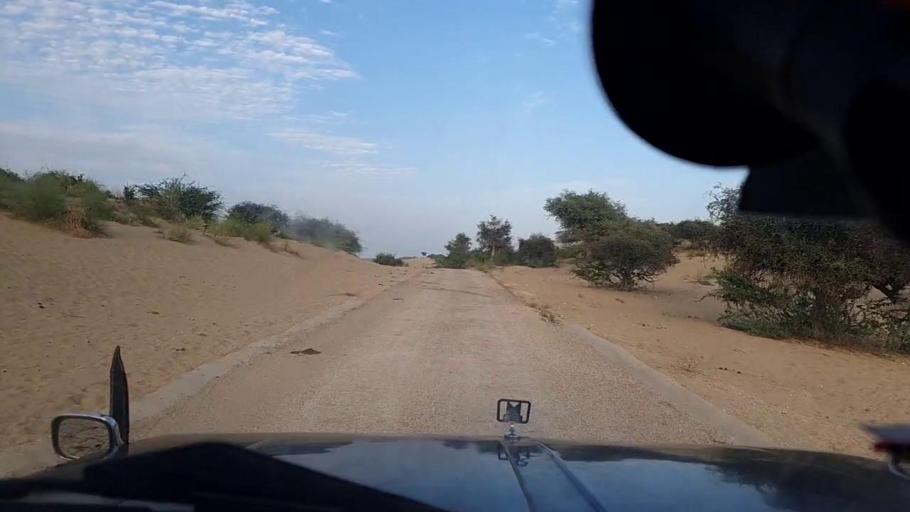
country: PK
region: Sindh
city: Diplo
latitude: 24.4694
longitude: 69.7904
